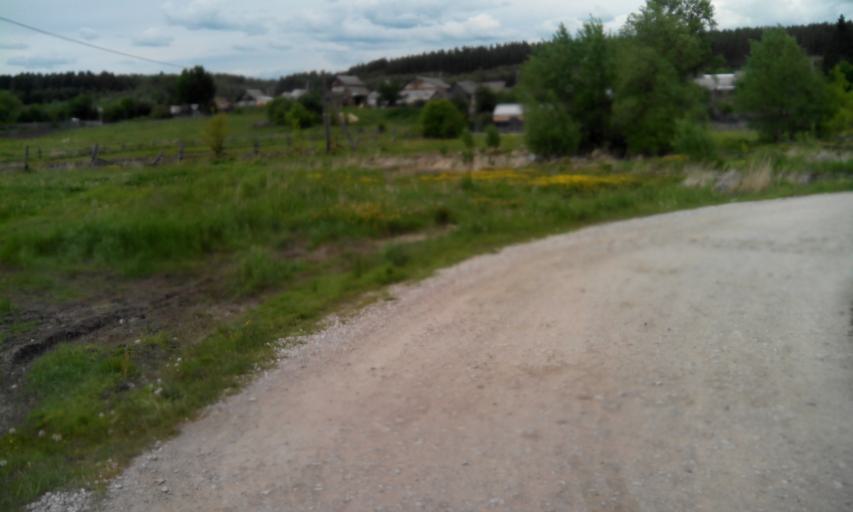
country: RU
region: Penza
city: Chaadayevka
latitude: 53.1825
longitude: 45.8610
